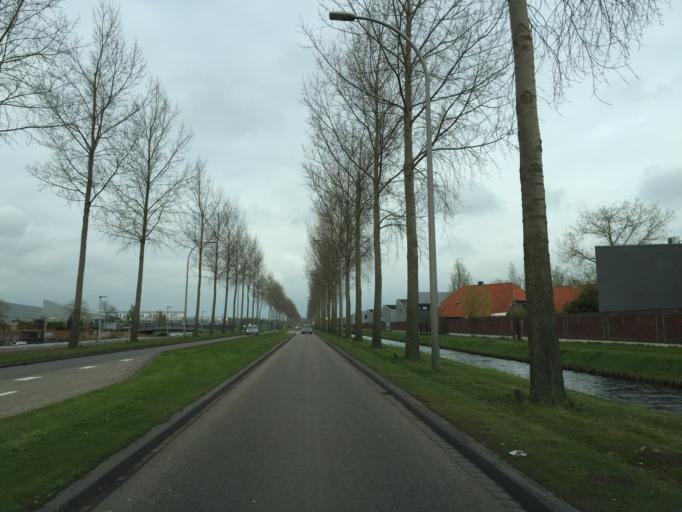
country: NL
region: South Holland
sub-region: Gemeente Den Haag
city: Ypenburg
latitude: 52.0308
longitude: 4.3645
